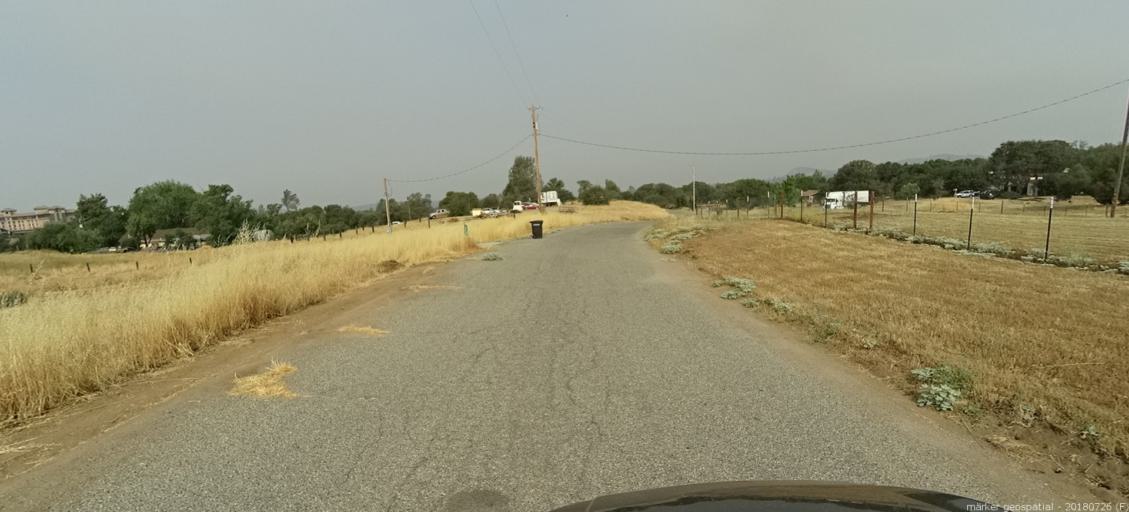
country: US
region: California
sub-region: Madera County
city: Coarsegold
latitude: 37.2155
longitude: -119.6950
